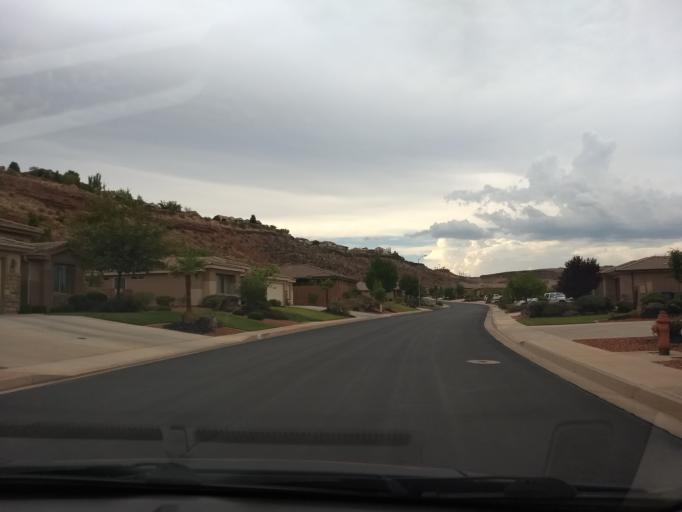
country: US
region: Utah
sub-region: Washington County
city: Saint George
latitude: 37.1080
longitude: -113.5469
